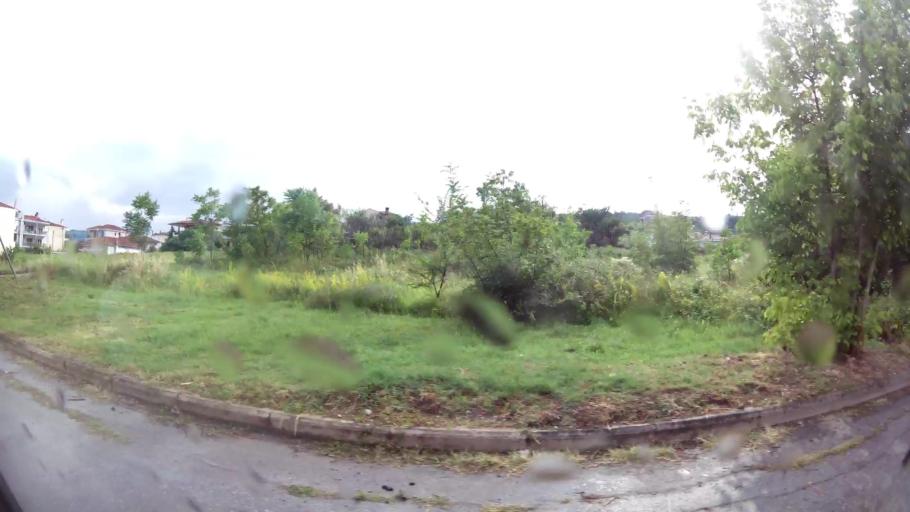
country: GR
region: Central Macedonia
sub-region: Nomos Imathias
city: Veroia
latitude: 40.5395
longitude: 22.2005
